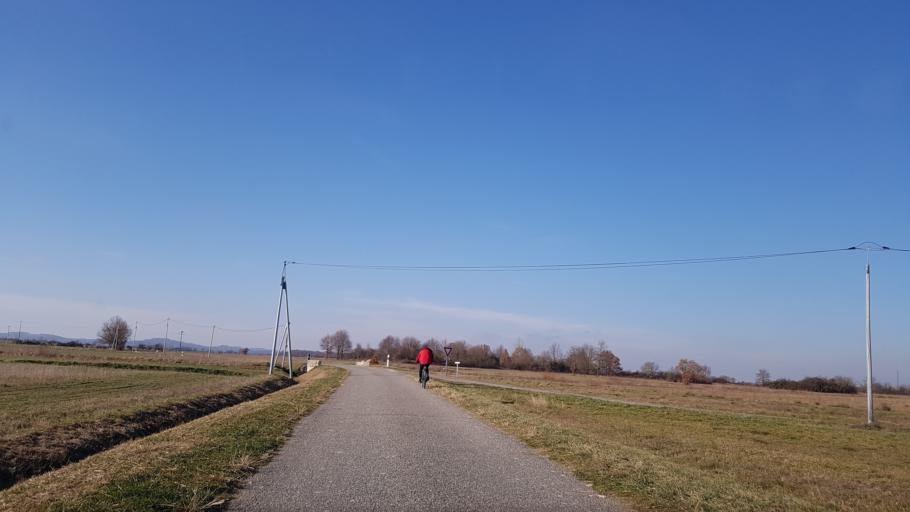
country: FR
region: Midi-Pyrenees
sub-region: Departement de l'Ariege
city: La Tour-du-Crieu
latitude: 43.1548
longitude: 1.6909
